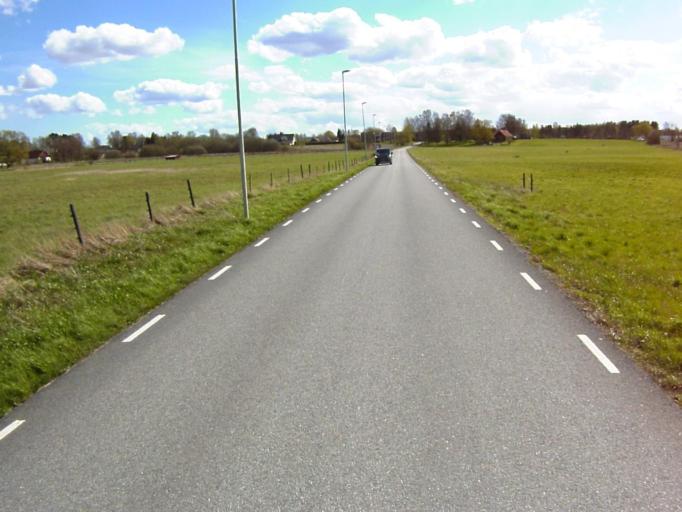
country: SE
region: Skane
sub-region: Kristianstads Kommun
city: Kristianstad
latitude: 56.0151
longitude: 14.0905
